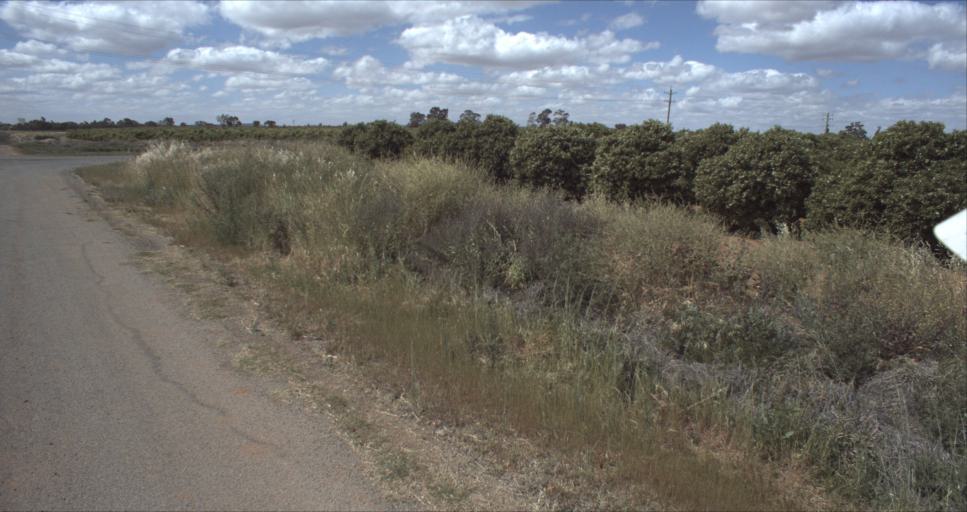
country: AU
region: New South Wales
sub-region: Leeton
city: Leeton
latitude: -34.5807
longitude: 146.3923
